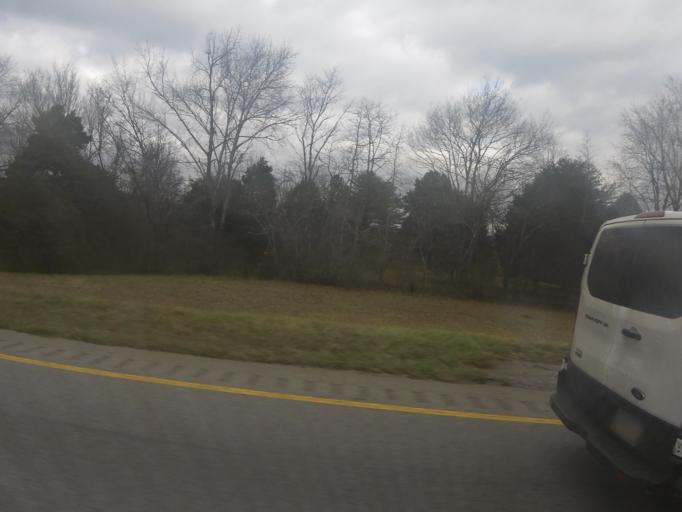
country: US
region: Tennessee
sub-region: Marion County
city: Jasper
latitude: 35.0390
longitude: -85.6014
